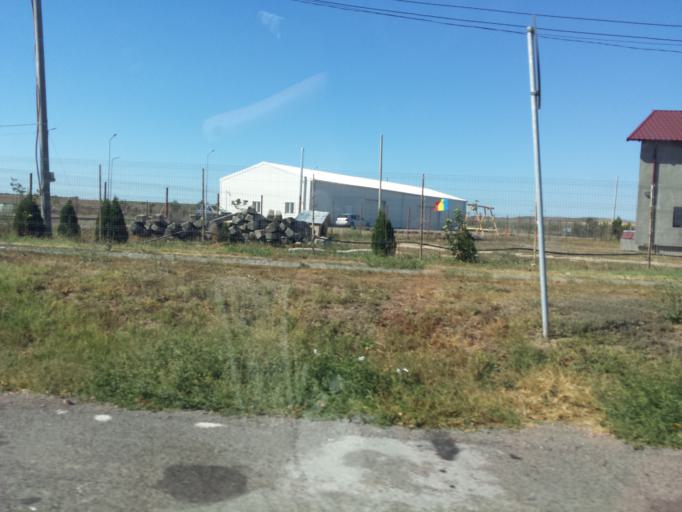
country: RO
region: Tulcea
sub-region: Comuna Frecatei
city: Cataloi
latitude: 45.1047
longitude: 28.7428
